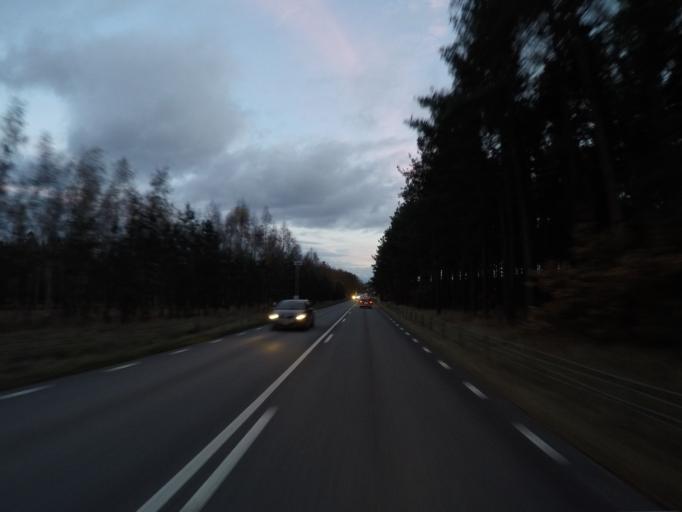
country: SE
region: Skane
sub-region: Kristianstads Kommun
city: Degeberga
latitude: 55.8167
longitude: 14.1300
